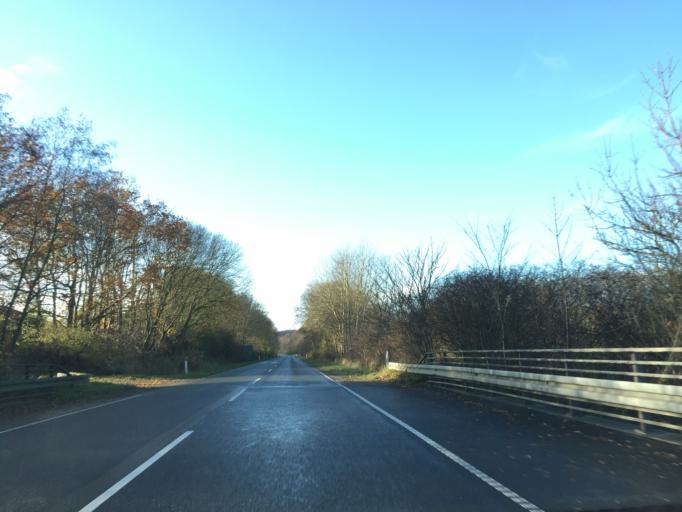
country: DK
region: Central Jutland
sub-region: Arhus Kommune
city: Framlev
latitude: 56.1858
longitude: 10.0045
